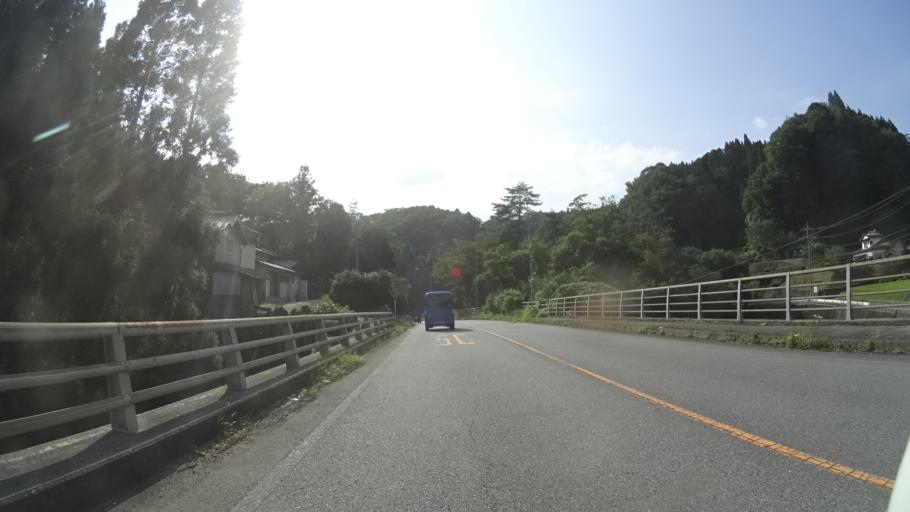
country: JP
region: Kumamoto
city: Aso
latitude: 32.6853
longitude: 131.0459
